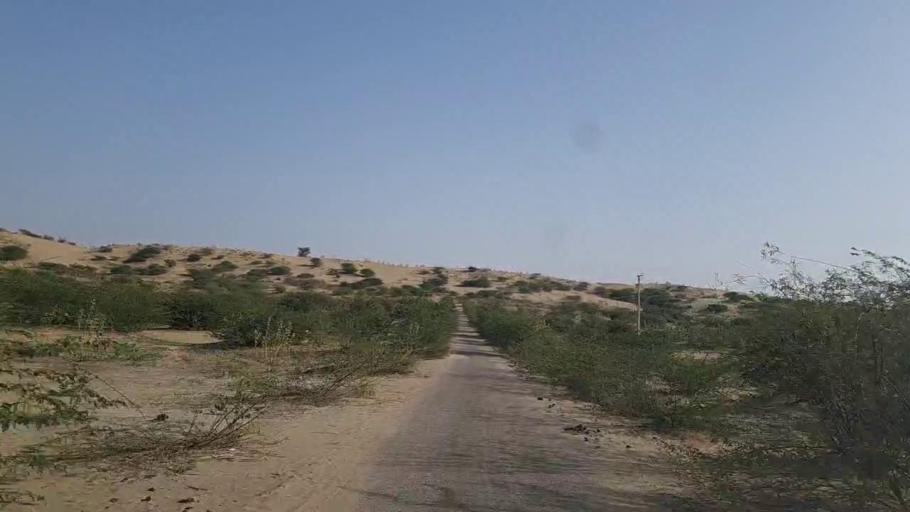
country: PK
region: Sindh
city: Naukot
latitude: 24.6205
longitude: 69.3712
